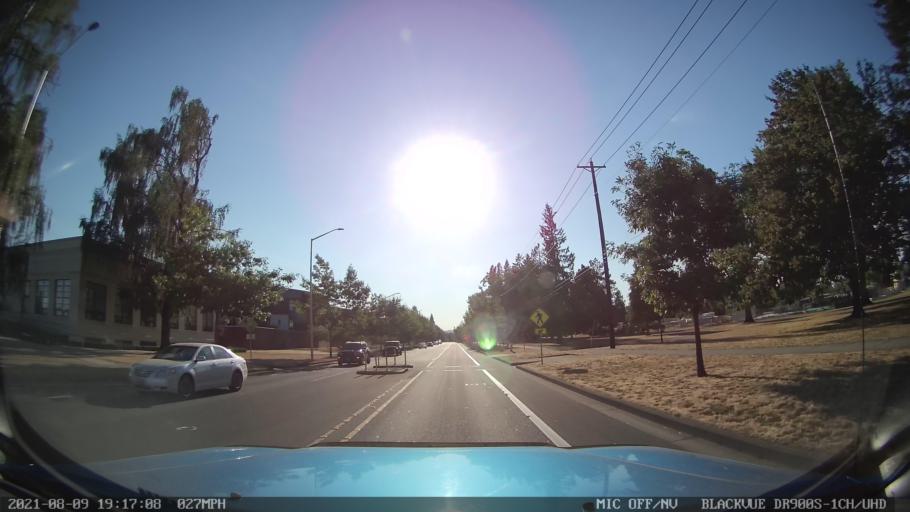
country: US
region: Oregon
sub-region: Marion County
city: Four Corners
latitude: 44.9399
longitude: -123.0005
